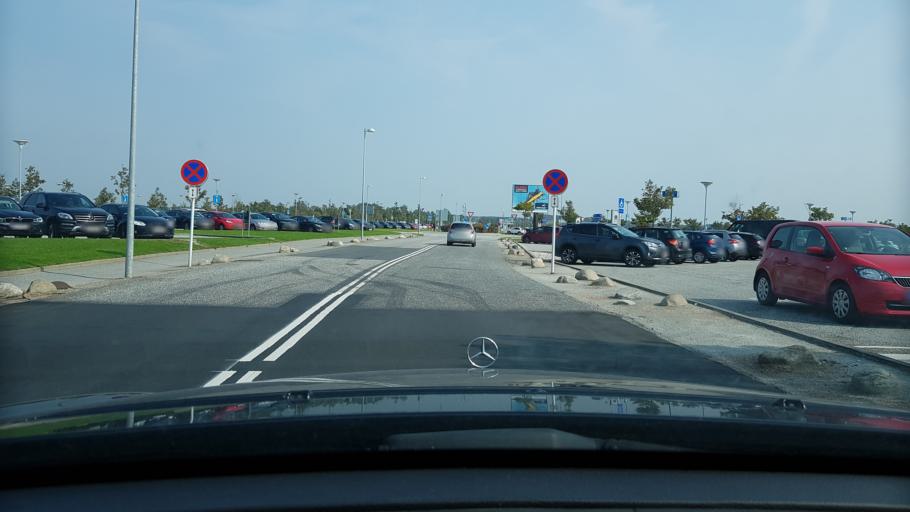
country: DK
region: North Denmark
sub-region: Alborg Kommune
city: Vadum
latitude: 57.0867
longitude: 9.8733
